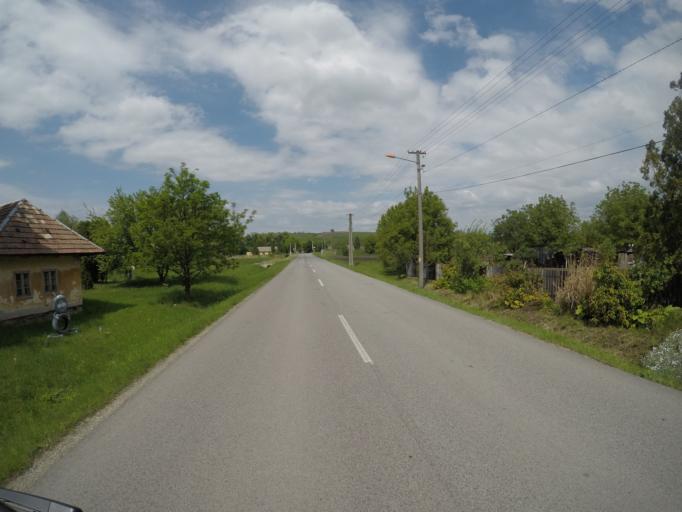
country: SK
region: Nitriansky
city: Zeliezovce
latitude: 47.9947
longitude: 18.7741
